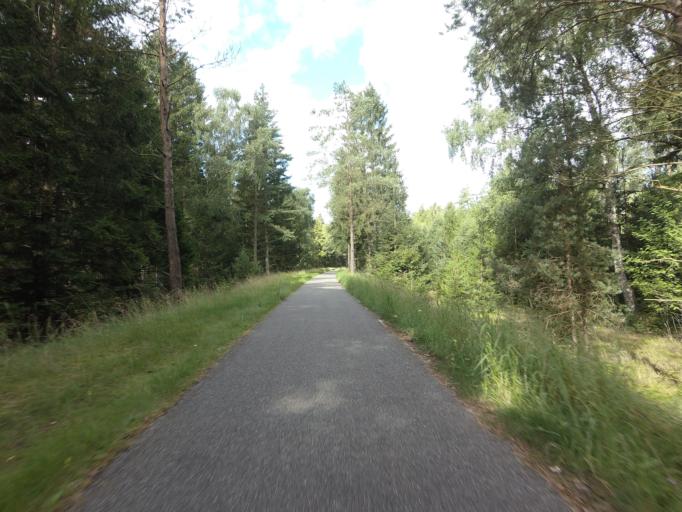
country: DK
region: Central Jutland
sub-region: Silkeborg Kommune
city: Silkeborg
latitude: 56.1655
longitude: 9.5927
